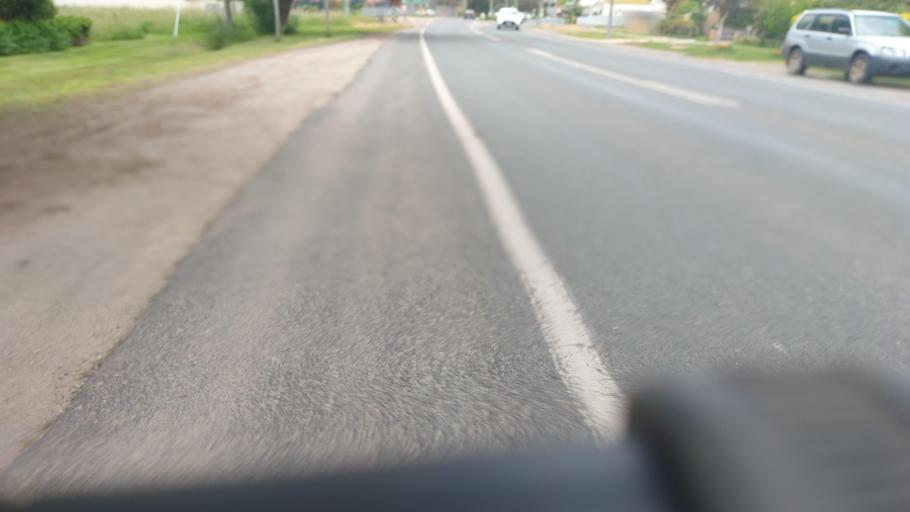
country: AU
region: Victoria
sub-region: Mount Alexander
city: Castlemaine
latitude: -37.0739
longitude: 144.2056
